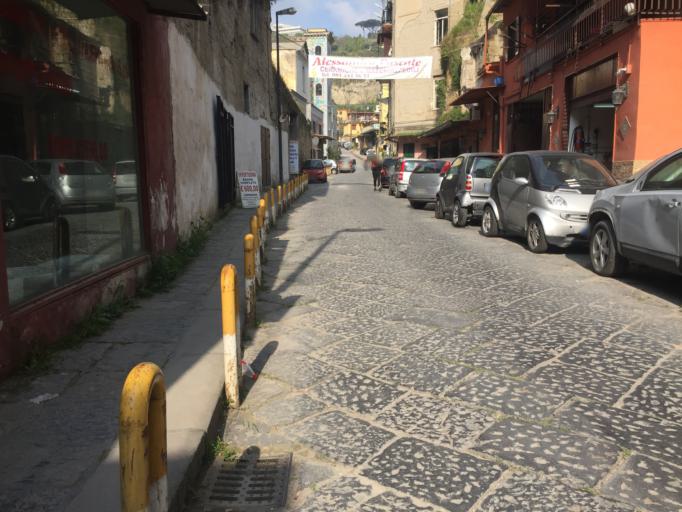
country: IT
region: Campania
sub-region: Provincia di Napoli
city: Napoli
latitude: 40.8587
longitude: 14.2401
